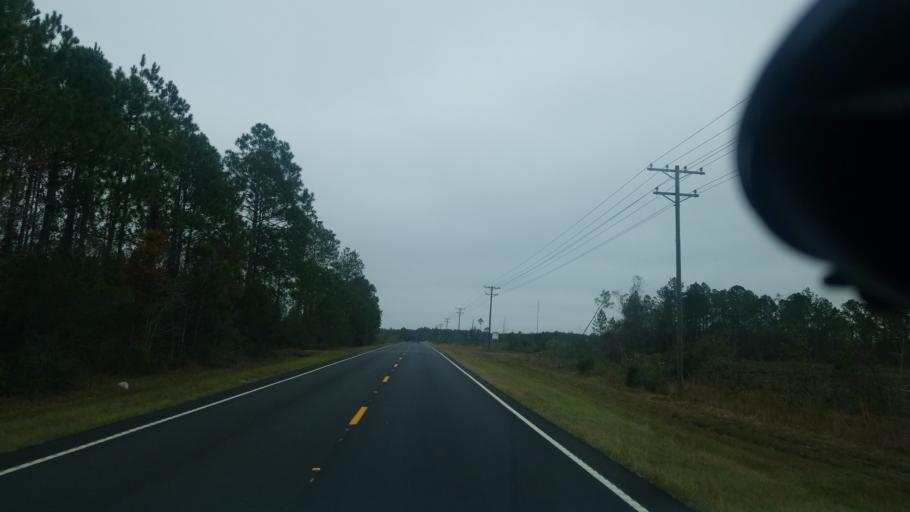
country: US
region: Florida
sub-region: Nassau County
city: Hilliard
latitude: 30.5218
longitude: -82.0654
